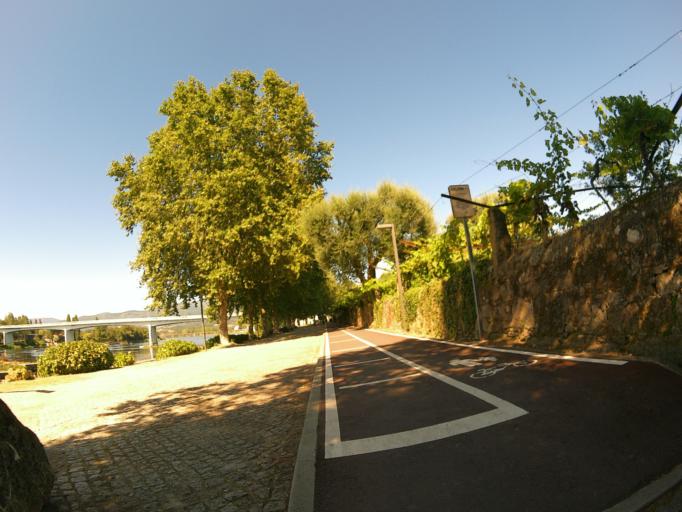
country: PT
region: Viana do Castelo
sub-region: Ponte de Lima
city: Ponte de Lima
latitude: 41.7622
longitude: -8.5922
